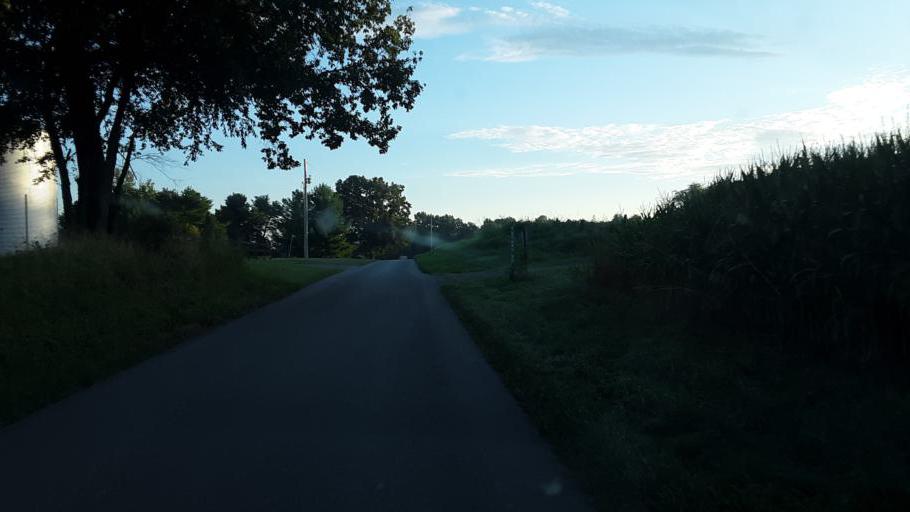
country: US
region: Kentucky
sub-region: Todd County
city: Guthrie
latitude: 36.6894
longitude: -87.1710
